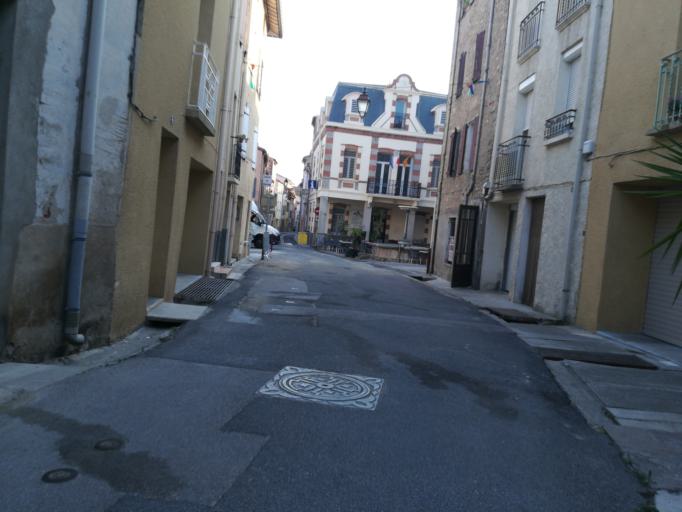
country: FR
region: Languedoc-Roussillon
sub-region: Departement des Pyrenees-Orientales
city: Maureillas-las-Illas
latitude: 42.4896
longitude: 2.8068
